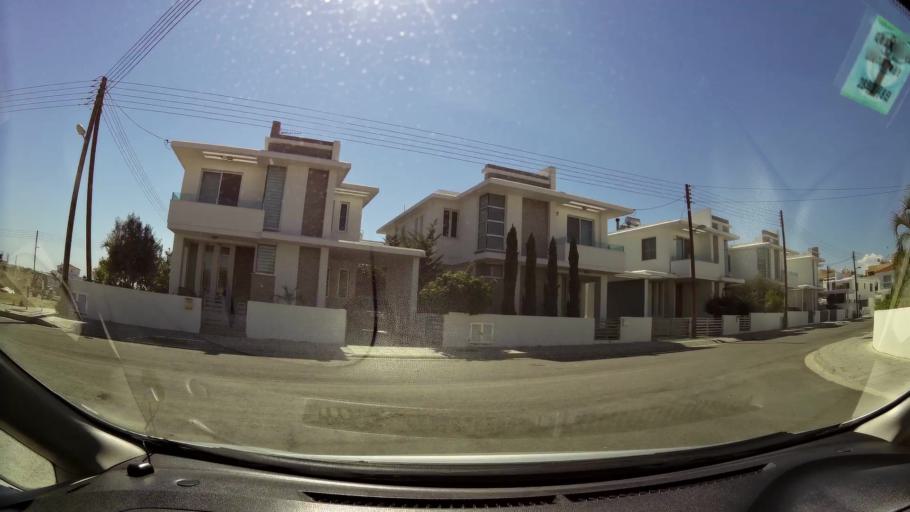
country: CY
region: Larnaka
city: Livadia
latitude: 34.9635
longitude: 33.6410
